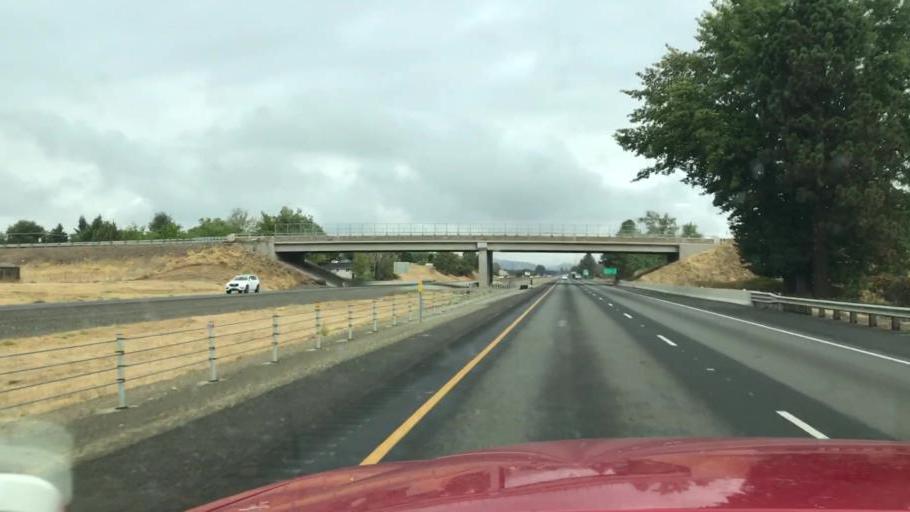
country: US
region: Oregon
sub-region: Jackson County
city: Central Point
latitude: 42.3892
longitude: -122.9182
